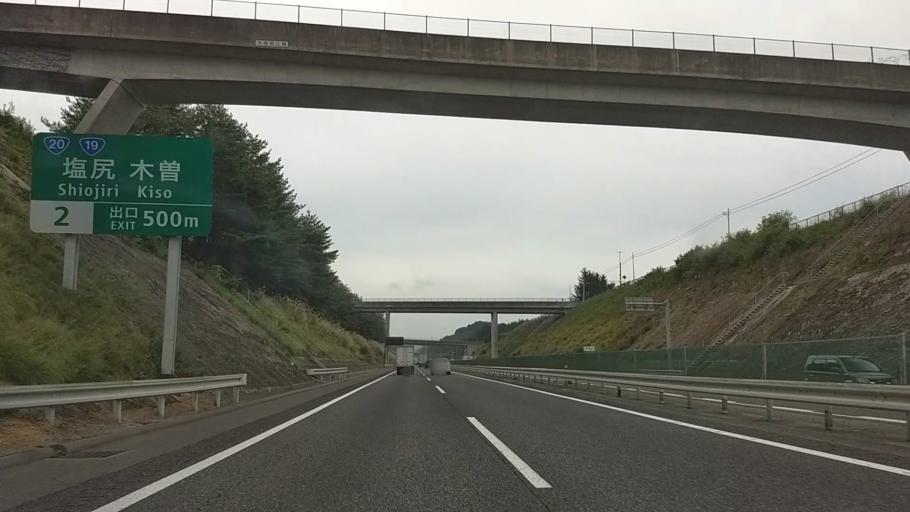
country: JP
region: Nagano
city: Shiojiri
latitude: 36.1235
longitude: 137.9783
